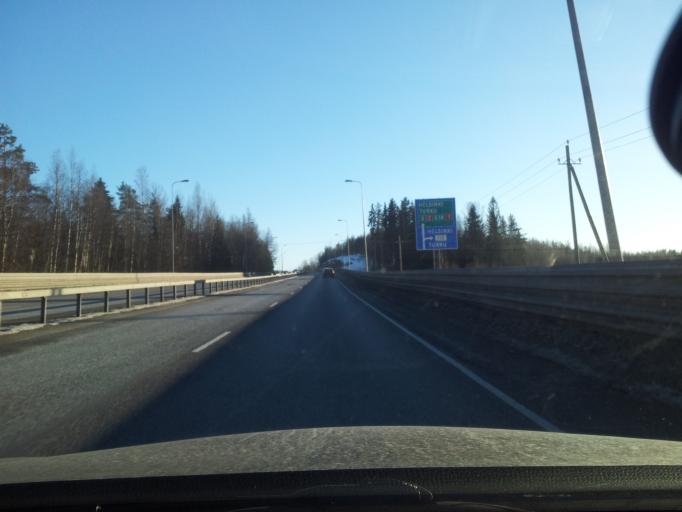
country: FI
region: Uusimaa
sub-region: Helsinki
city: Vihti
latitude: 60.3099
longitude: 24.3495
